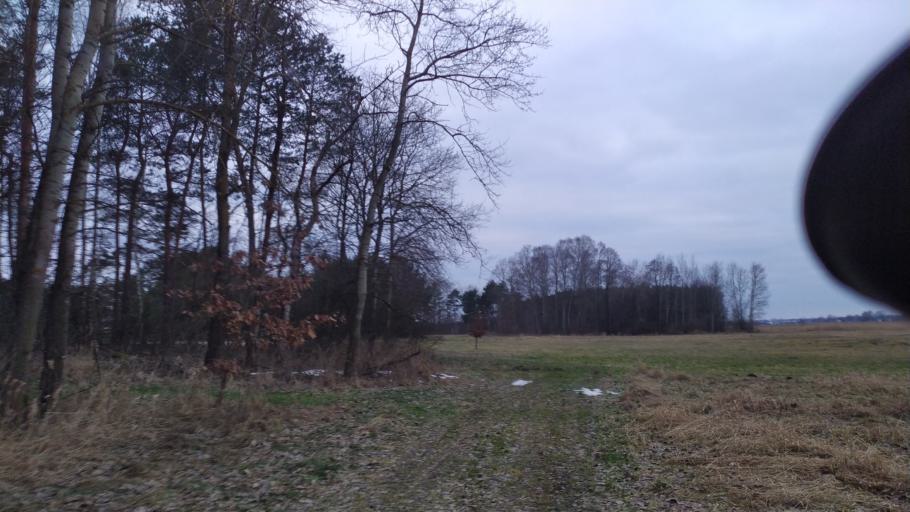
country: PL
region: Lublin Voivodeship
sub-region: Powiat lubartowski
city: Abramow
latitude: 51.4303
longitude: 22.2905
